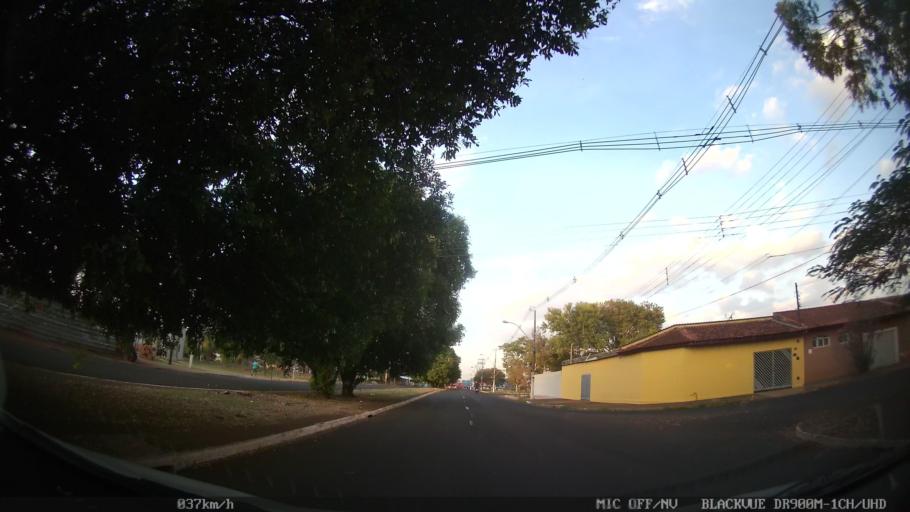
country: BR
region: Sao Paulo
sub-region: Ribeirao Preto
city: Ribeirao Preto
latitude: -21.1264
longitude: -47.8288
